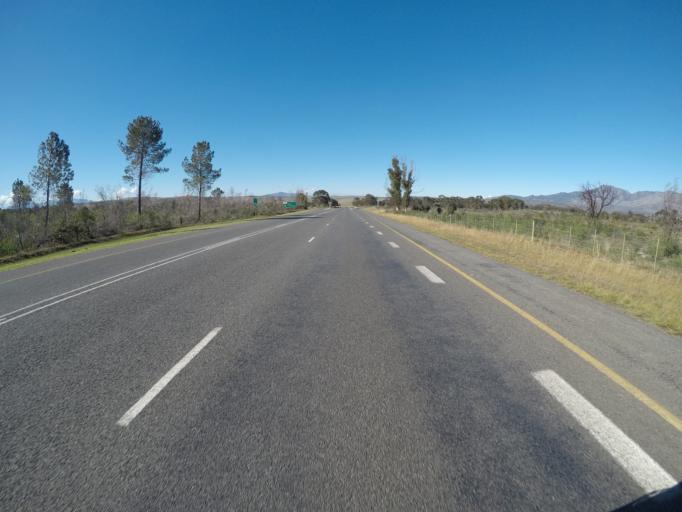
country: ZA
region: Western Cape
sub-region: Overberg District Municipality
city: Hermanus
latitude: -34.2352
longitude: 19.1971
